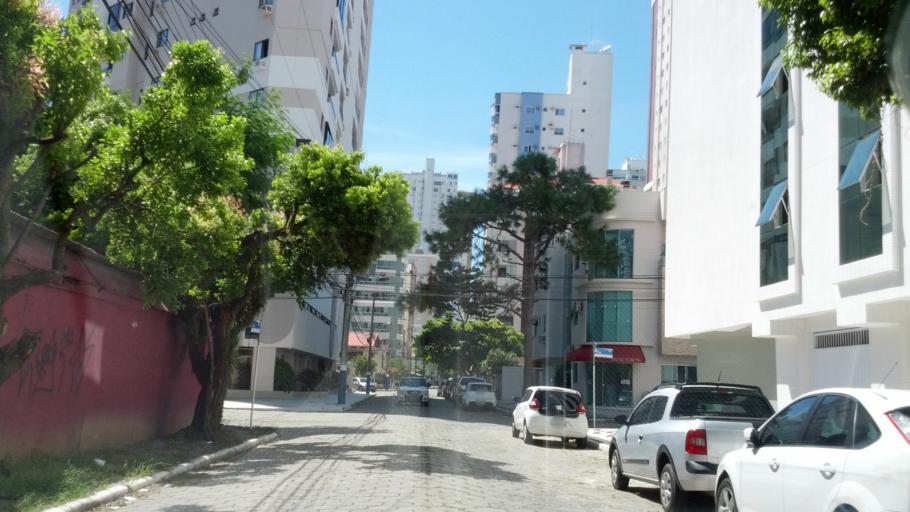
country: BR
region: Santa Catarina
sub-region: Balneario Camboriu
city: Balneario Camboriu
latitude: -27.0002
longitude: -48.6294
